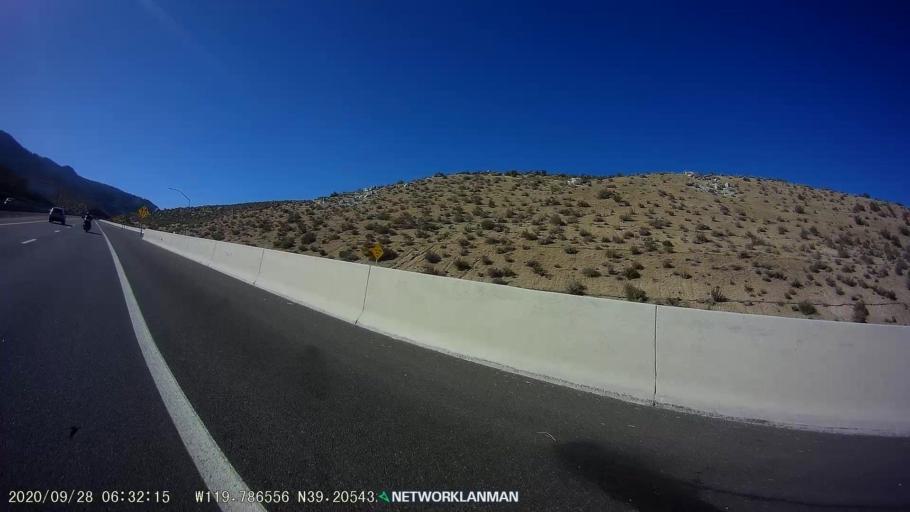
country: US
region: Nevada
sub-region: Carson City
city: Carson City
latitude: 39.2055
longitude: -119.7872
